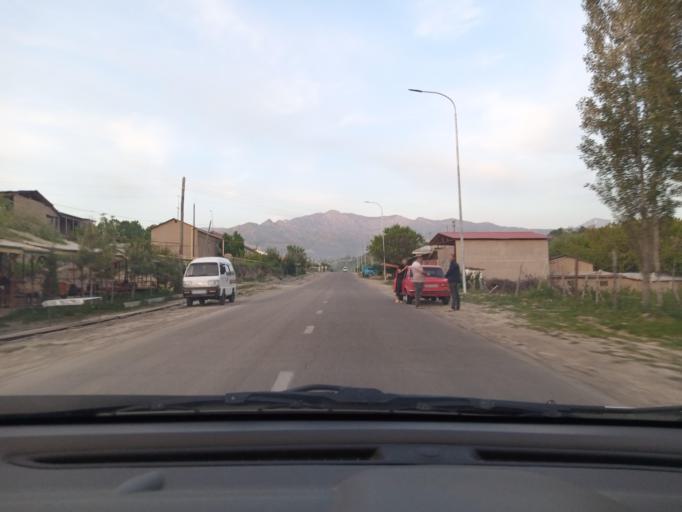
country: UZ
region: Toshkent
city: Parkent
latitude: 41.2451
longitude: 69.7443
